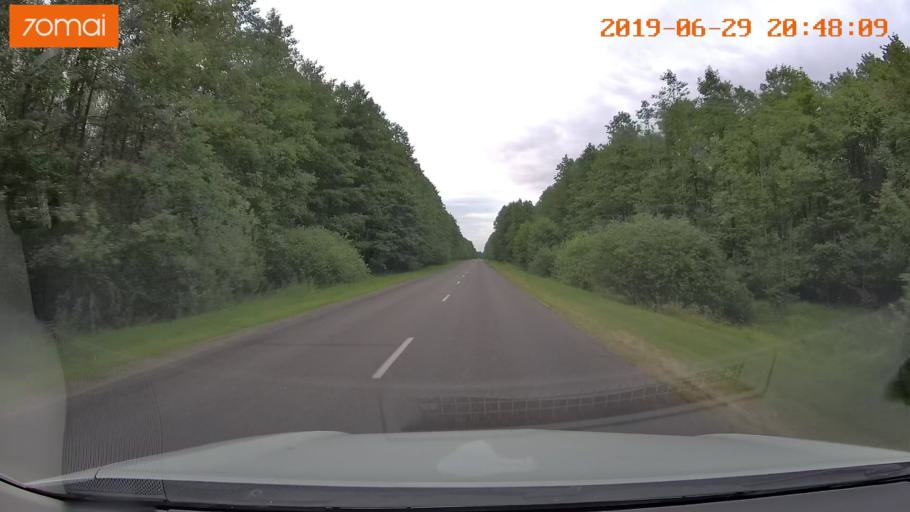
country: BY
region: Brest
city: Hantsavichy
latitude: 52.6467
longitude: 26.3170
